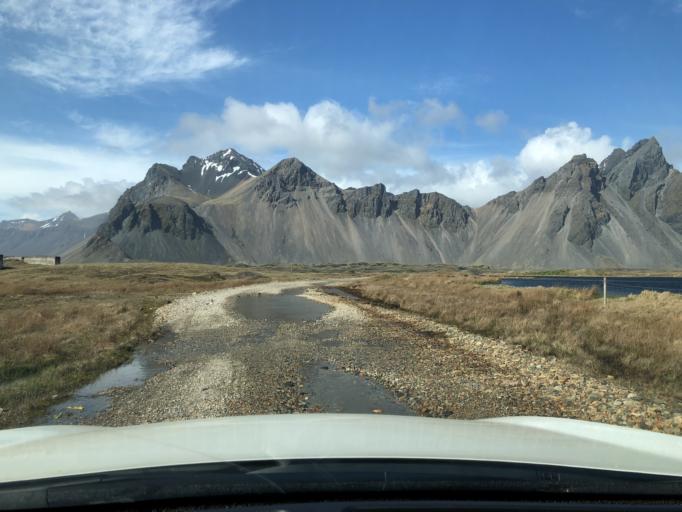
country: IS
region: East
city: Hoefn
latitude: 64.2410
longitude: -14.9716
